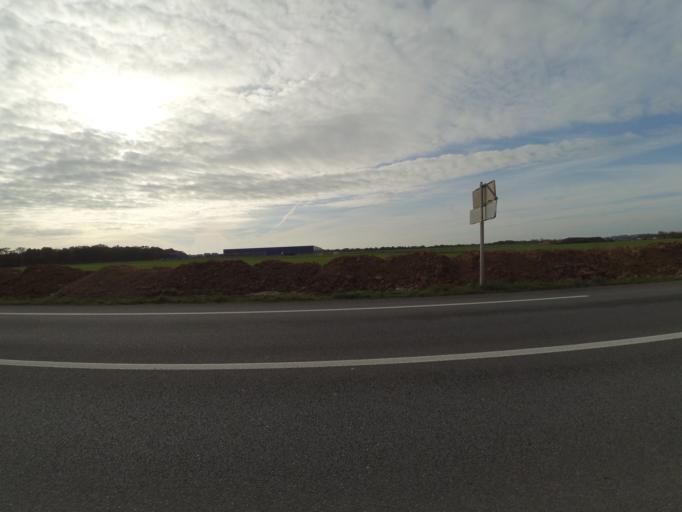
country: FR
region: Pays de la Loire
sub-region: Departement de la Vendee
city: Saint-Hilaire-de-Loulay
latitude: 47.0234
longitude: -1.3473
